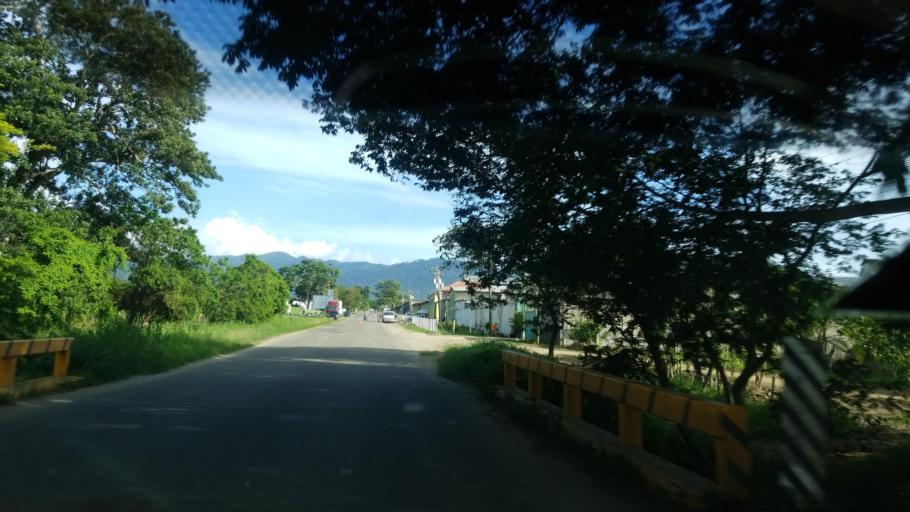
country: HN
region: El Paraiso
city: Cuyali
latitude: 13.8881
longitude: -86.5548
